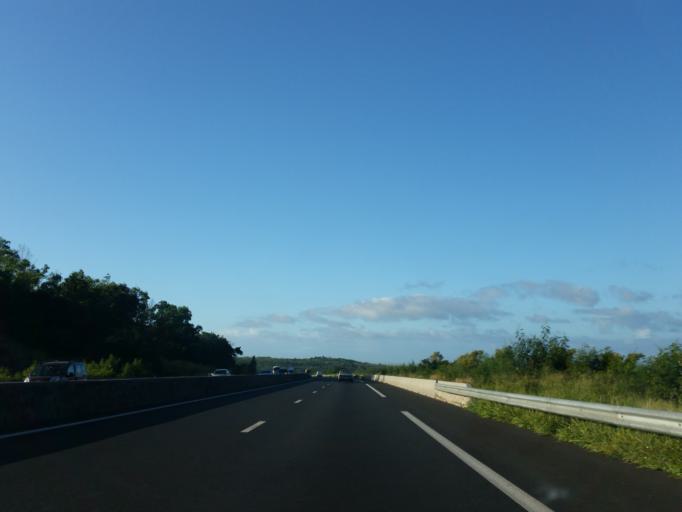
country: RE
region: Reunion
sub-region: Reunion
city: Les Avirons
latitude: -21.2517
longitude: 55.3275
